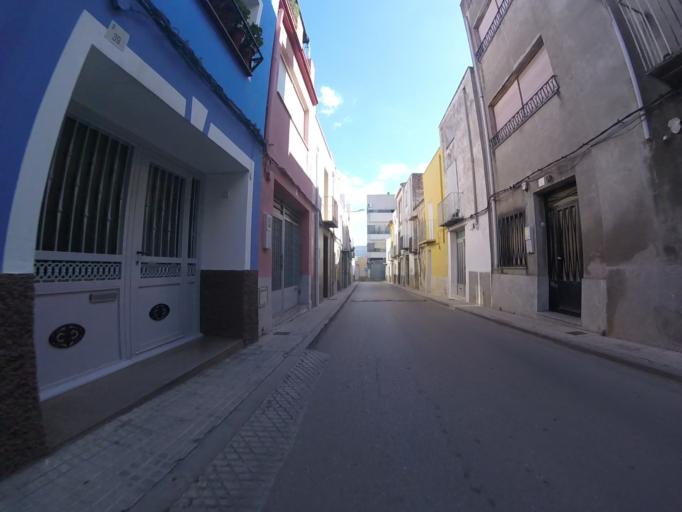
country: ES
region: Valencia
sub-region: Provincia de Castello
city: Alcala de Xivert
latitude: 40.3027
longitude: 0.2233
